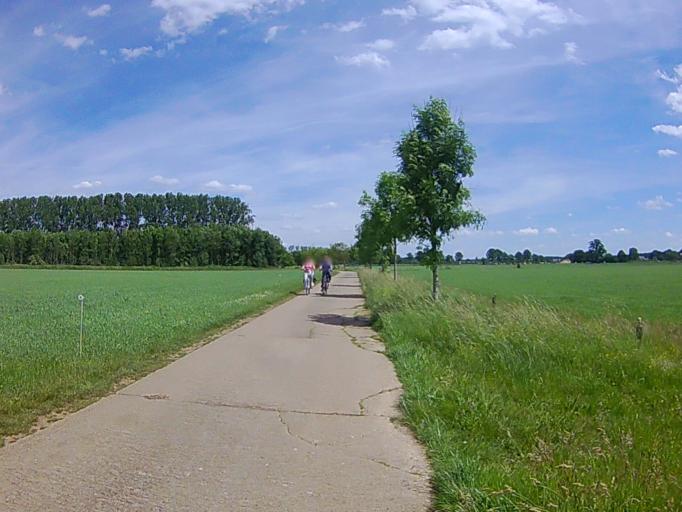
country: BE
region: Flanders
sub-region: Provincie Antwerpen
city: Lille
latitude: 51.2281
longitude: 4.8702
